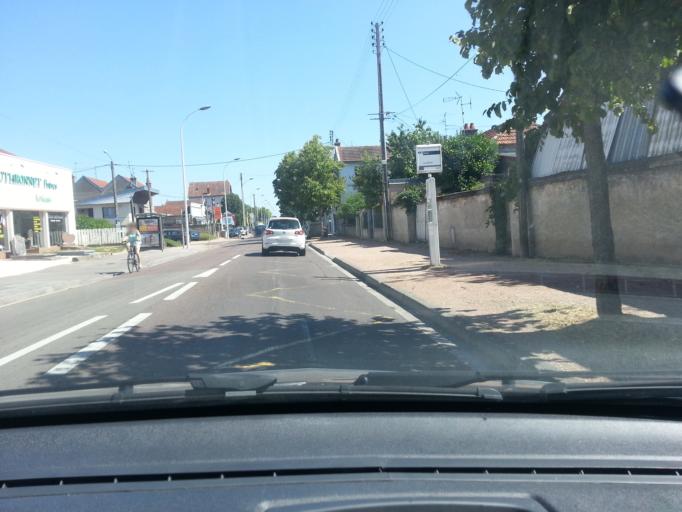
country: FR
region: Bourgogne
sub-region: Departement de la Cote-d'Or
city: Longvic
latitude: 47.3065
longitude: 5.0591
